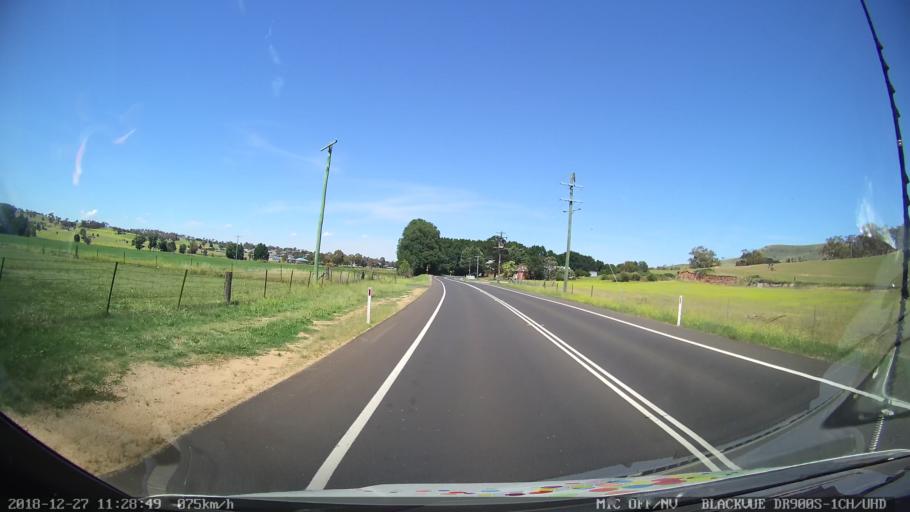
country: AU
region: New South Wales
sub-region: Bathurst Regional
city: Perthville
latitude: -33.4809
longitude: 149.5597
